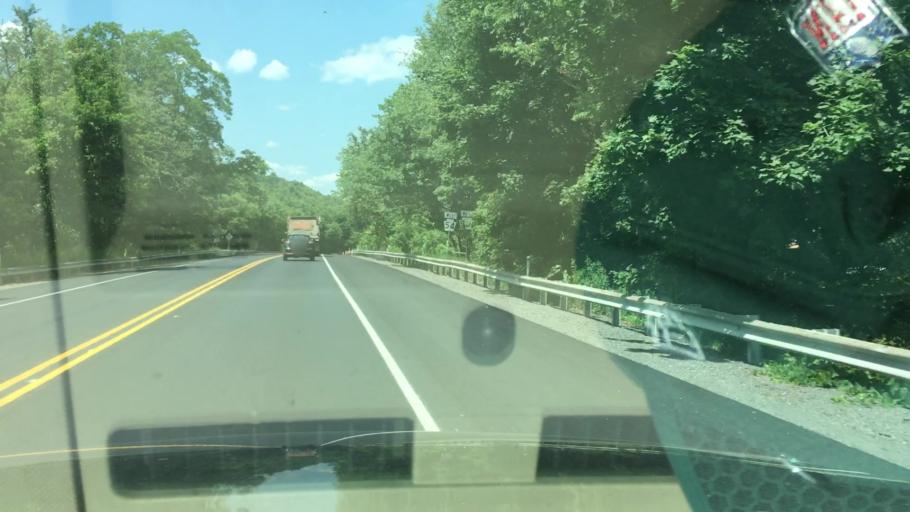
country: US
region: Pennsylvania
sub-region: Northumberland County
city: Kulpmont
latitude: 40.7718
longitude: -76.4423
